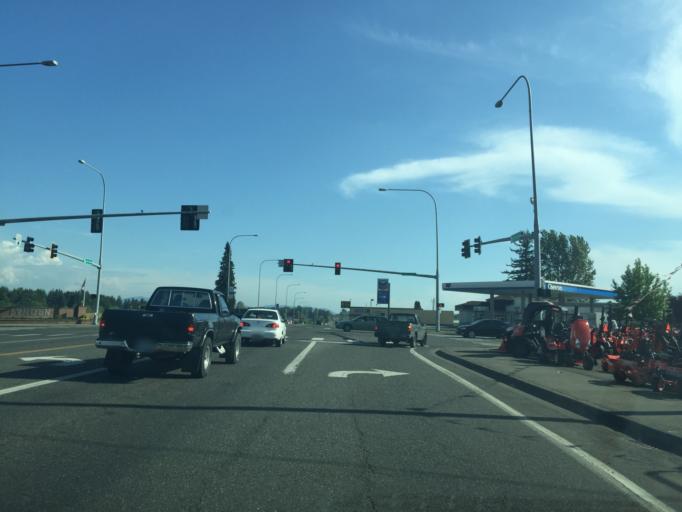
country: US
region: Washington
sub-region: Whatcom County
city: Lynden
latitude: 48.9396
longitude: -122.4855
